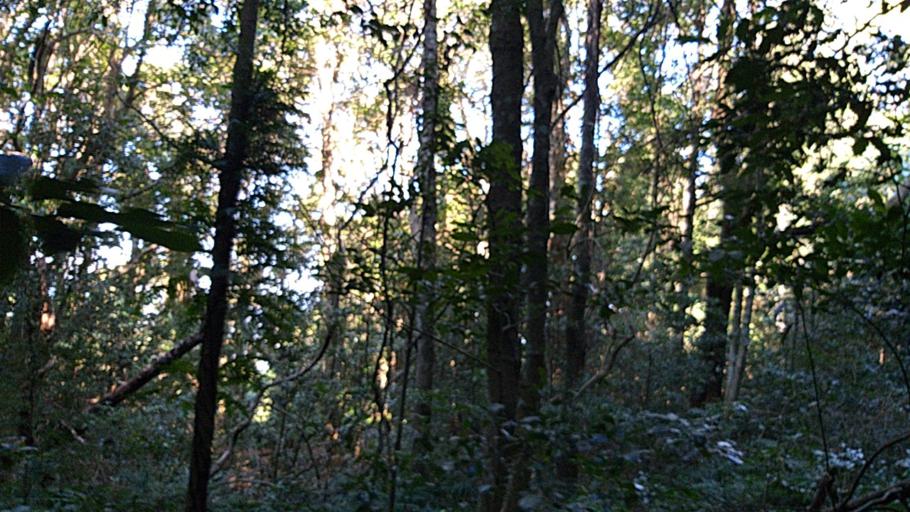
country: AU
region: New South Wales
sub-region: Wollongong
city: Mount Keira
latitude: -34.4052
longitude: 150.8575
